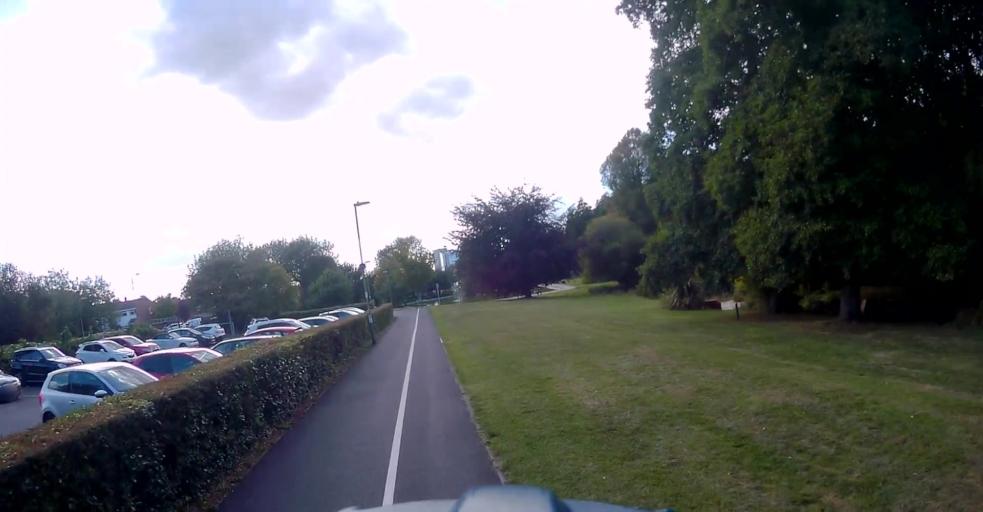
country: GB
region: England
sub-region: Hampshire
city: Basingstoke
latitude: 51.2667
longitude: -1.0721
